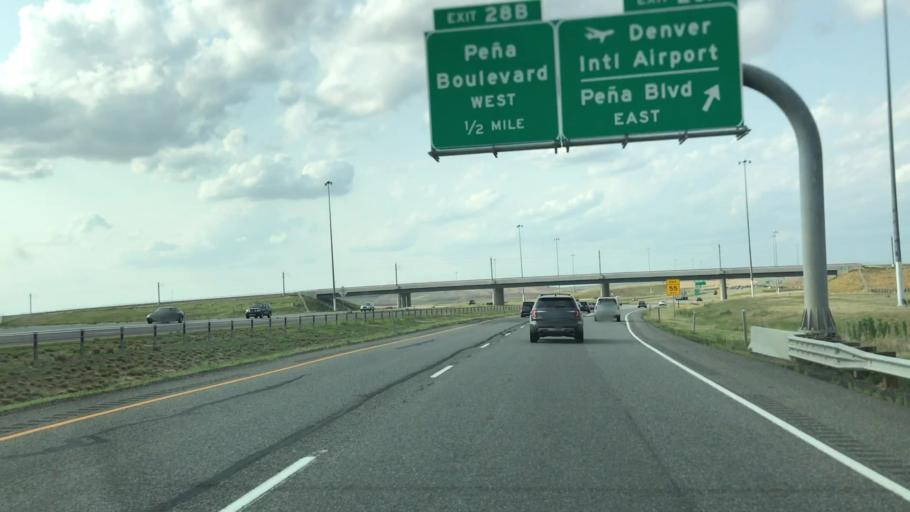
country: US
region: Colorado
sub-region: Adams County
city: Aurora
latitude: 39.8251
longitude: -104.7464
